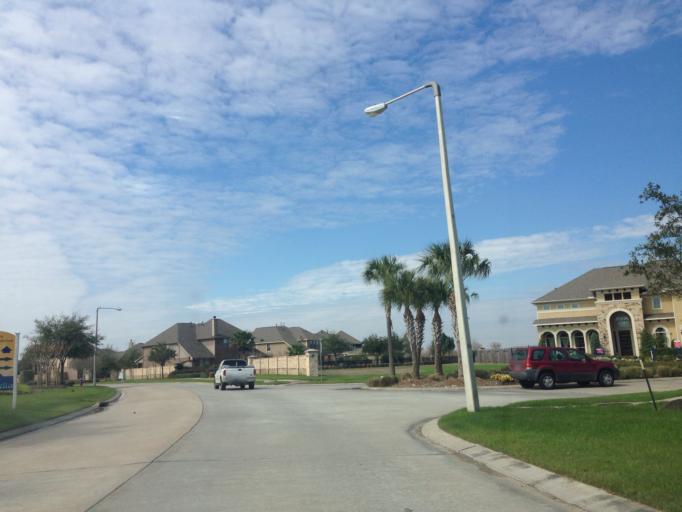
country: US
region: Texas
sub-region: Galveston County
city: Kemah
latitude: 29.5164
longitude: -95.0178
